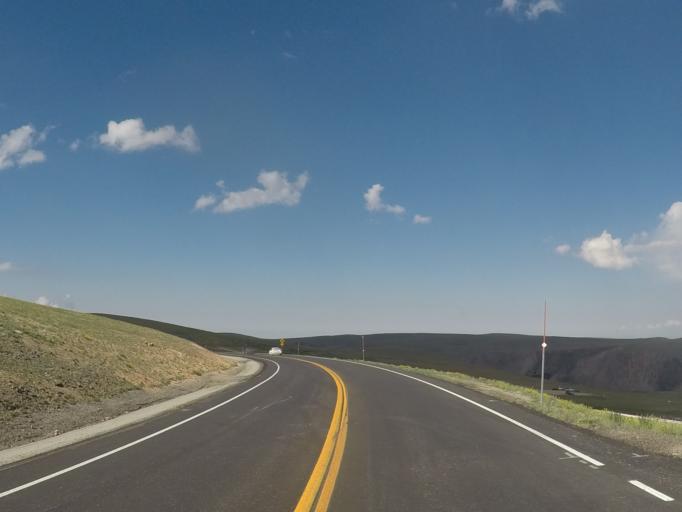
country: US
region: Montana
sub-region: Carbon County
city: Red Lodge
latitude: 45.0053
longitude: -109.4095
